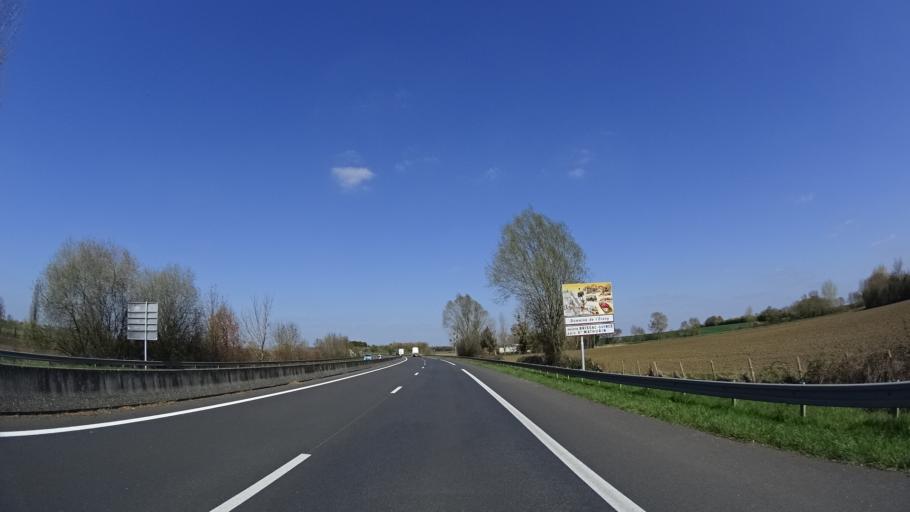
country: FR
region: Pays de la Loire
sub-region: Departement de Maine-et-Loire
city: Saint-Jean
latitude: 47.2422
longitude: -0.3209
